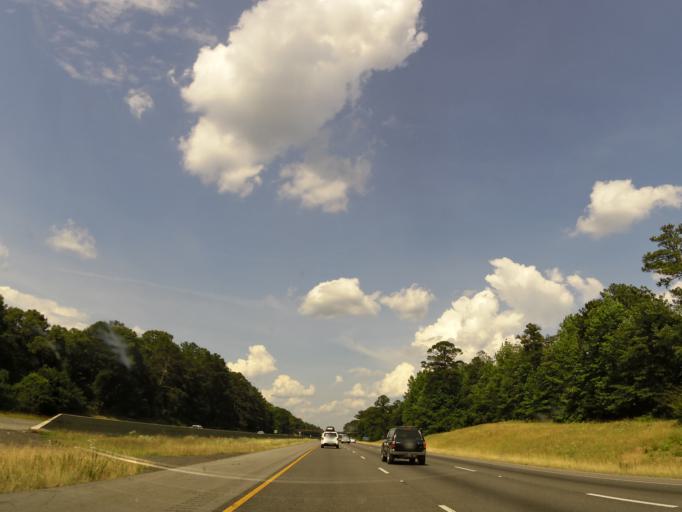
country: US
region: Alabama
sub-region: Tuscaloosa County
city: Coaling
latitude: 33.1866
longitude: -87.3335
